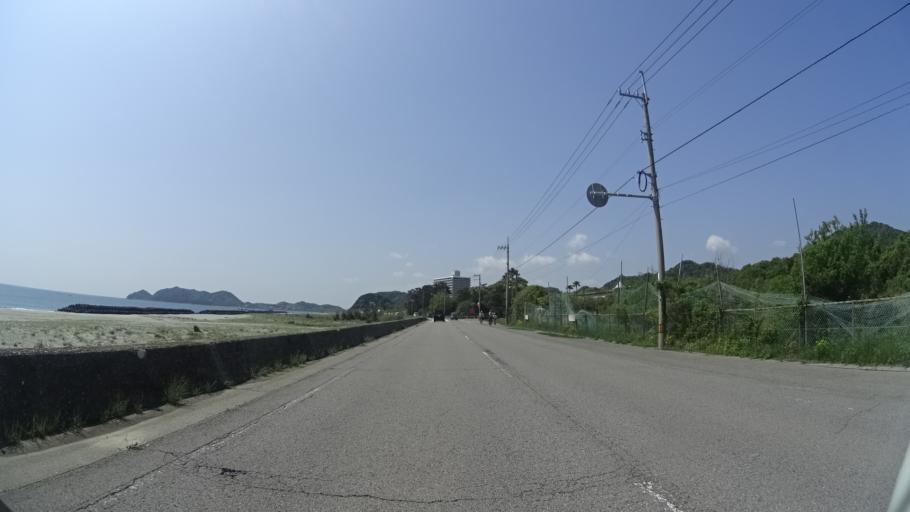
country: JP
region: Tokushima
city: Narutocho-mitsuishi
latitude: 34.2026
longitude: 134.6256
